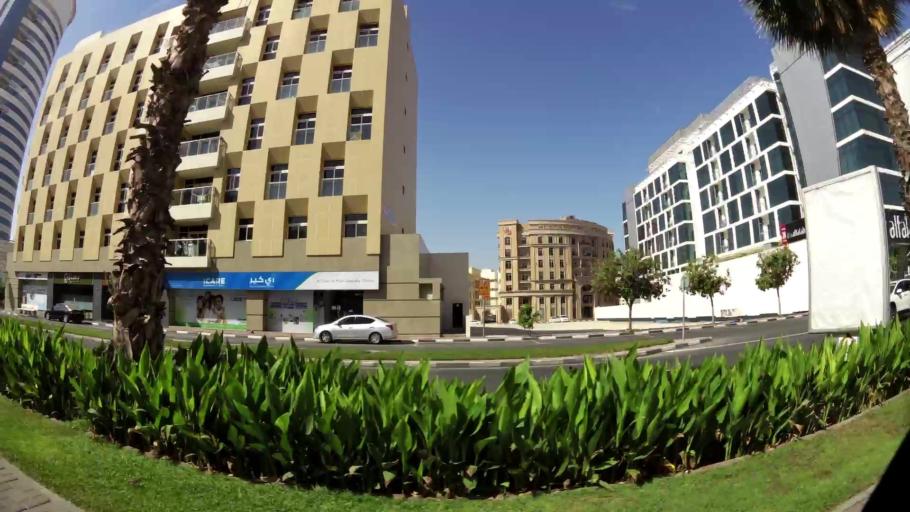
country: AE
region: Ash Shariqah
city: Sharjah
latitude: 25.2524
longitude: 55.2880
